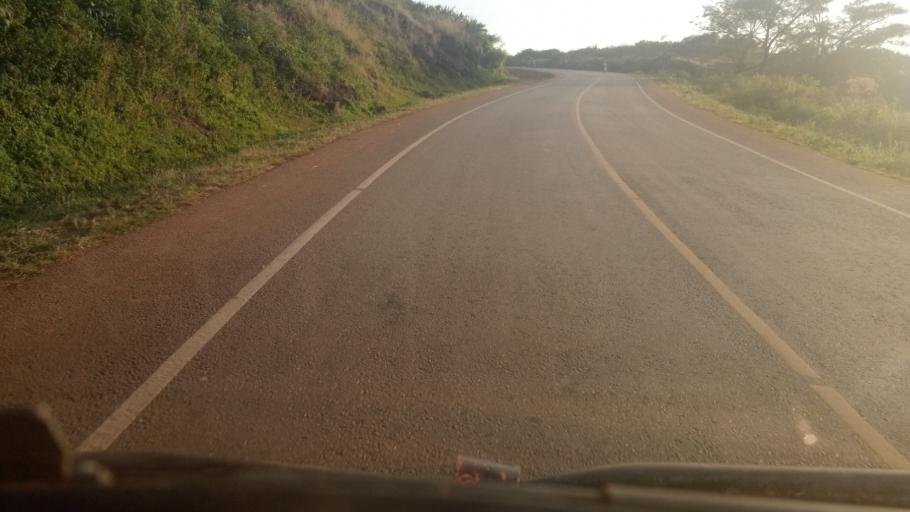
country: UG
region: Eastern Region
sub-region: Sironko District
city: Sironko
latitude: 1.3357
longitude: 34.3228
